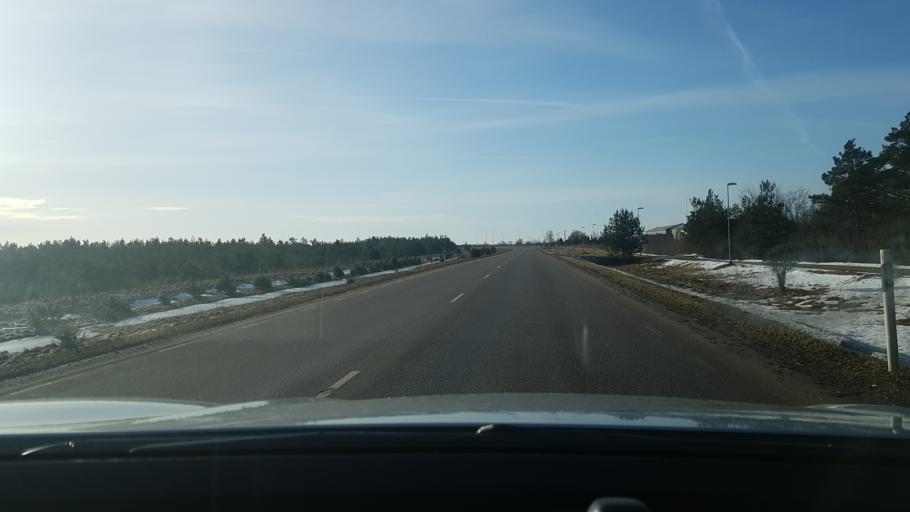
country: EE
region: Saare
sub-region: Kuressaare linn
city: Kuressaare
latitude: 58.2410
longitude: 22.5023
